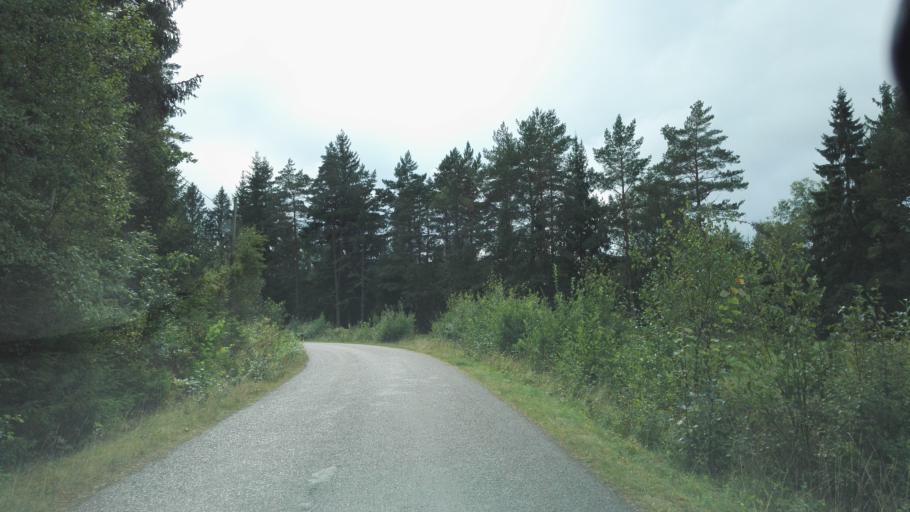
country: SE
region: Joenkoeping
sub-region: Vetlanda Kommun
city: Landsbro
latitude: 57.2151
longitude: 14.9538
